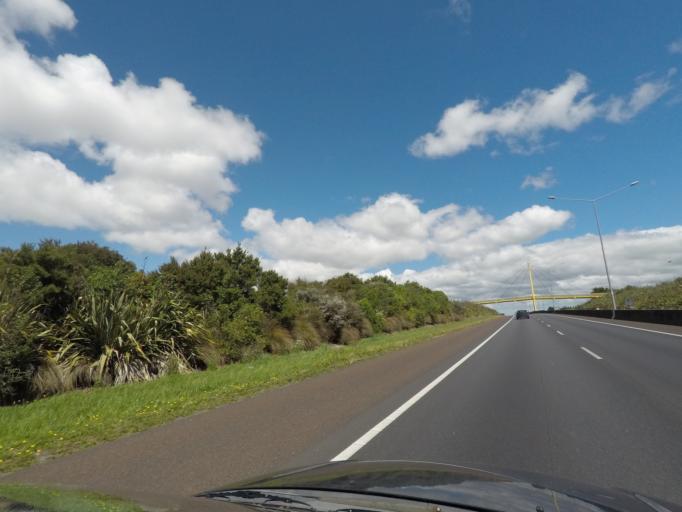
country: NZ
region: Auckland
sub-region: Auckland
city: Rosebank
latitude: -36.7945
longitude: 174.6490
